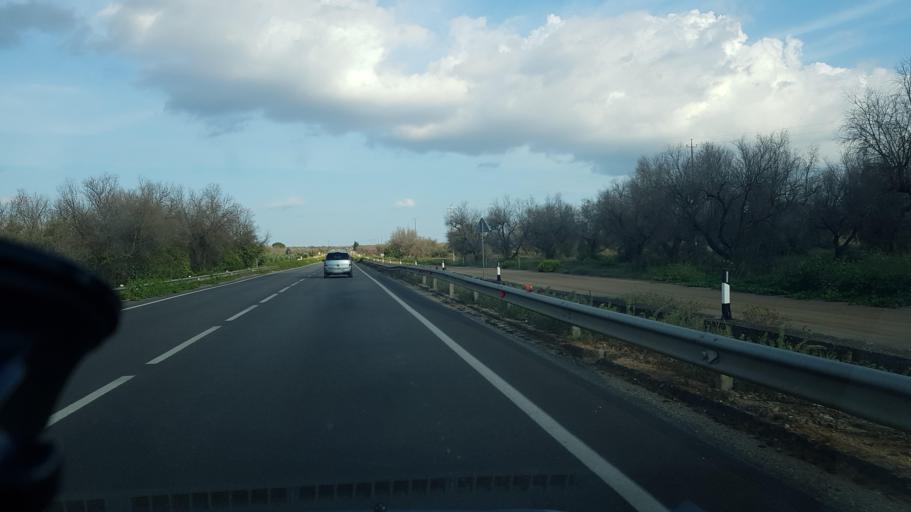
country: IT
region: Apulia
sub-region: Provincia di Lecce
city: Gemini
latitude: 39.9211
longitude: 18.1940
